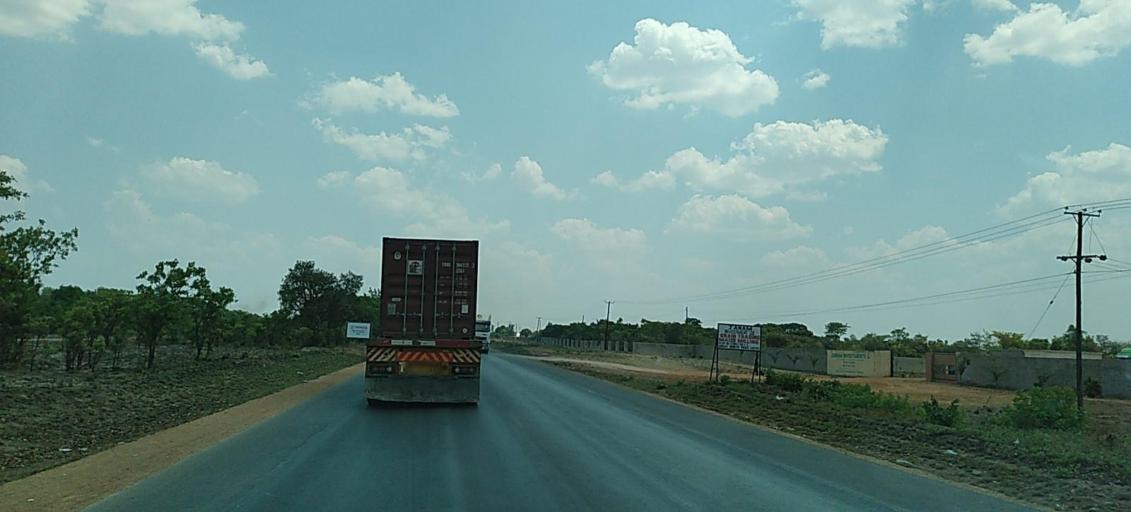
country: ZM
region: Central
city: Kabwe
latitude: -14.3692
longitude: 28.5093
